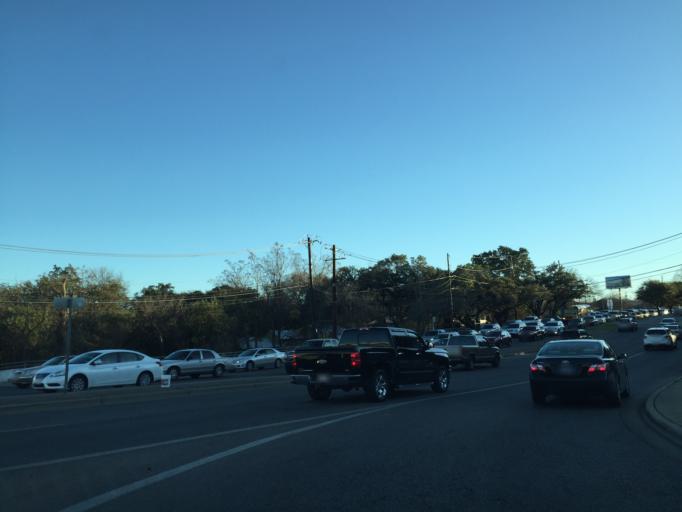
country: US
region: Texas
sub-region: Travis County
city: Austin
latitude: 30.3321
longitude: -97.6869
